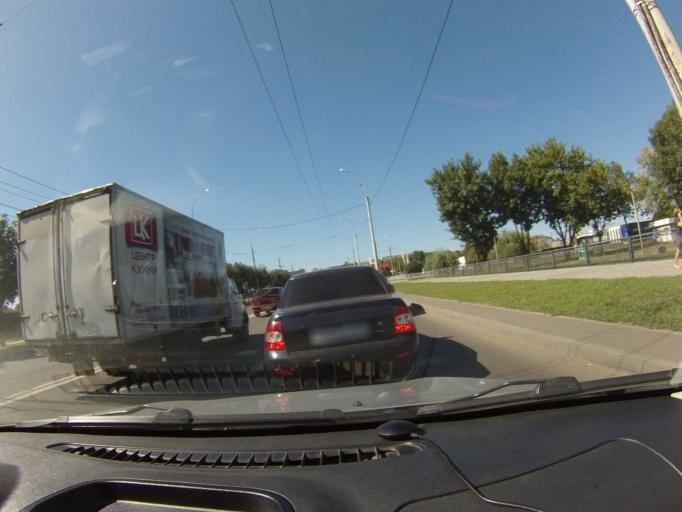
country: RU
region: Tambov
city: Tambov
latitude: 52.7582
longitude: 41.4424
